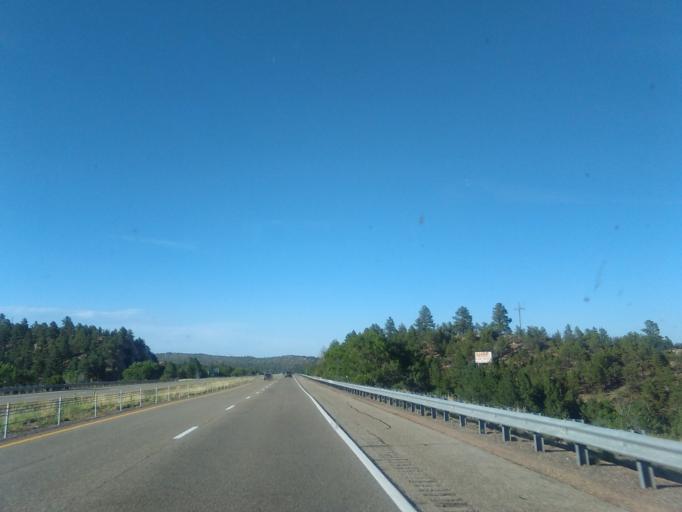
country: US
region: New Mexico
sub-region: San Miguel County
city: Las Vegas
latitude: 35.5067
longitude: -105.2593
